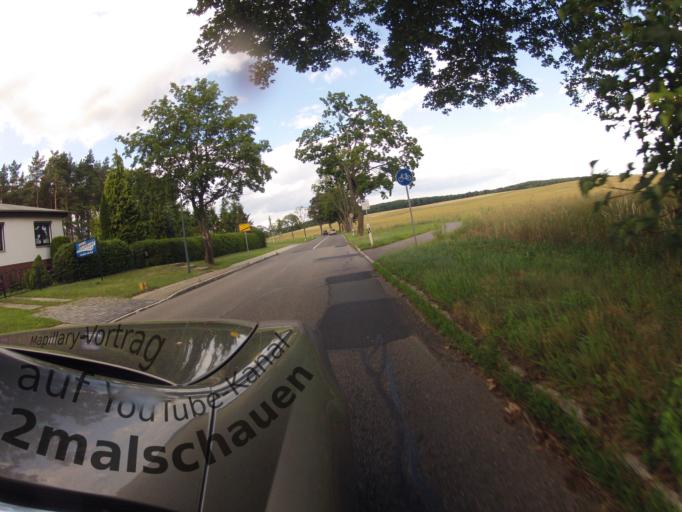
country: DE
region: Mecklenburg-Vorpommern
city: Seebad Heringsdorf
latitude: 53.8943
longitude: 14.1435
